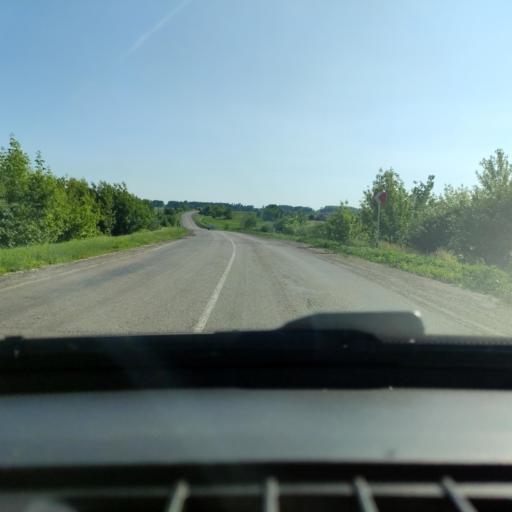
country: RU
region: Voronezj
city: Panino
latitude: 51.6125
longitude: 40.0063
